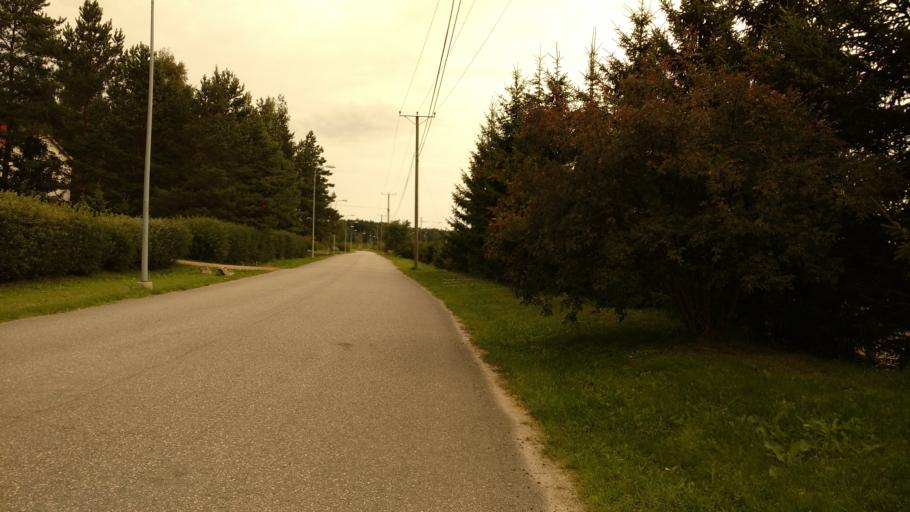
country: FI
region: Varsinais-Suomi
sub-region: Turku
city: Piikkioe
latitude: 60.4315
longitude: 22.5431
